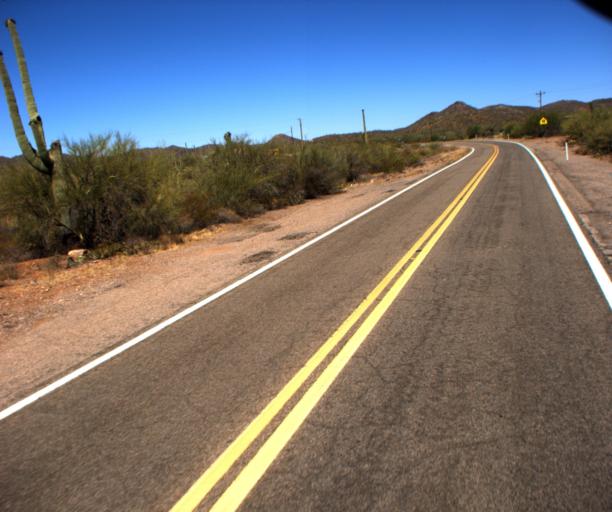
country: US
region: Arizona
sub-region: Pima County
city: Sells
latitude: 32.1675
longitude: -112.1282
